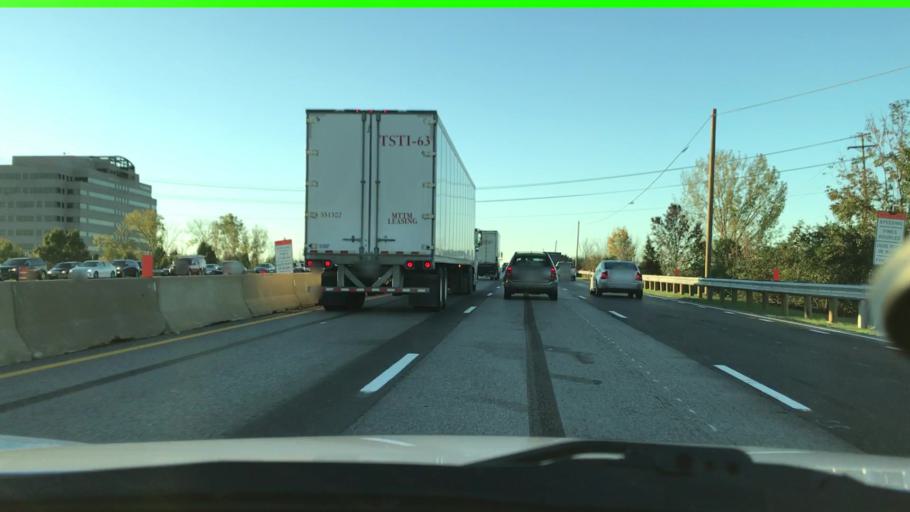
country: US
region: Ohio
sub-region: Franklin County
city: Hilliard
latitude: 40.0264
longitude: -83.1224
